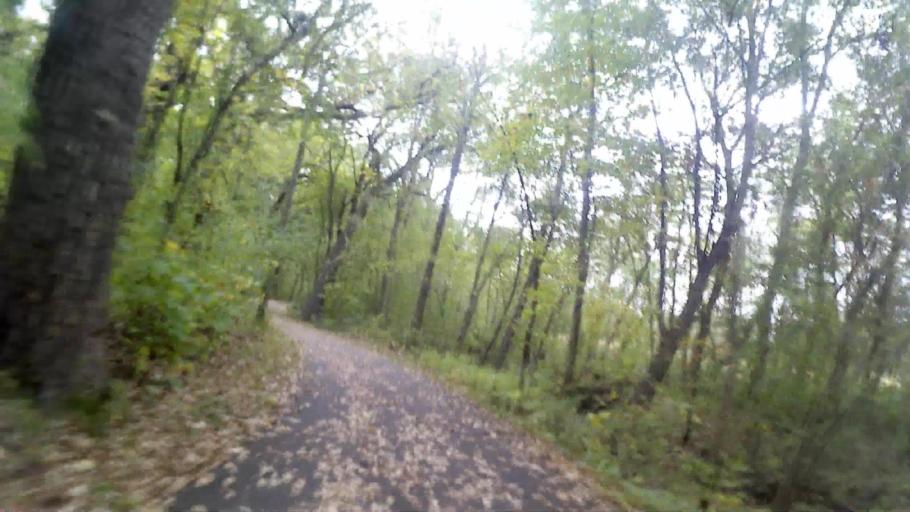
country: US
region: Illinois
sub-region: Kane County
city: Sugar Grove
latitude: 41.7816
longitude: -88.4301
